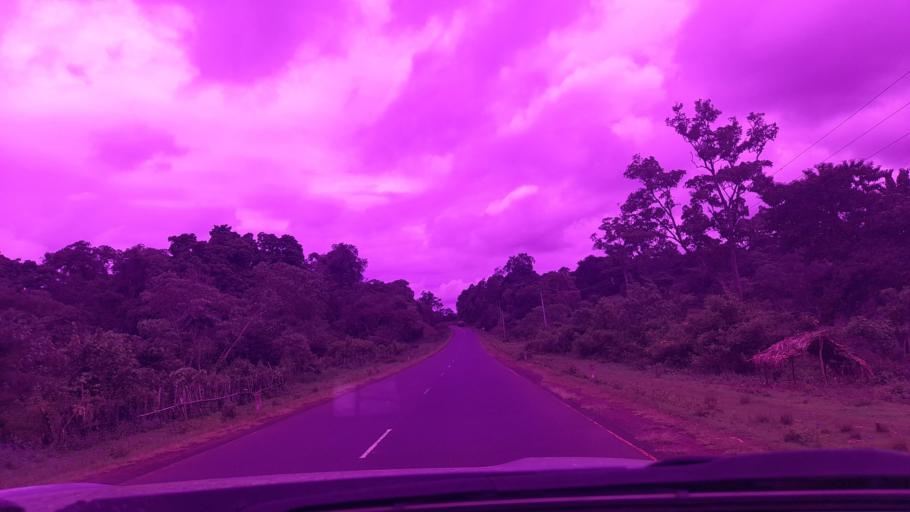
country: ET
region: Southern Nations, Nationalities, and People's Region
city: Bonga
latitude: 7.2800
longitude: 35.9473
